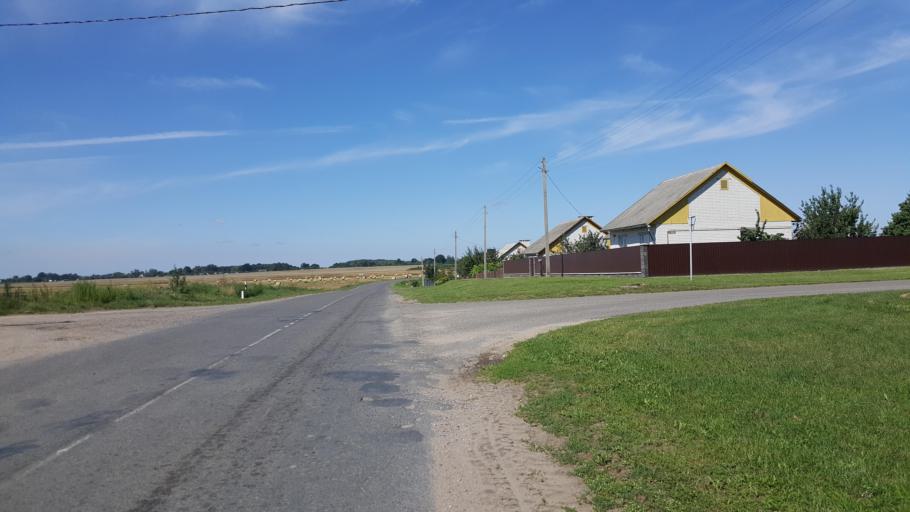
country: BY
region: Brest
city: Charnawchytsy
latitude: 52.2734
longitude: 23.7588
